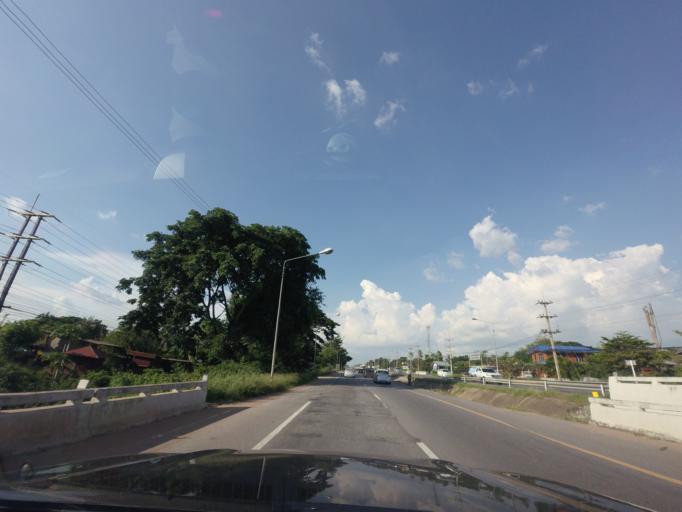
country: TH
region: Khon Kaen
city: Ban Phai
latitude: 16.0593
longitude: 102.7166
